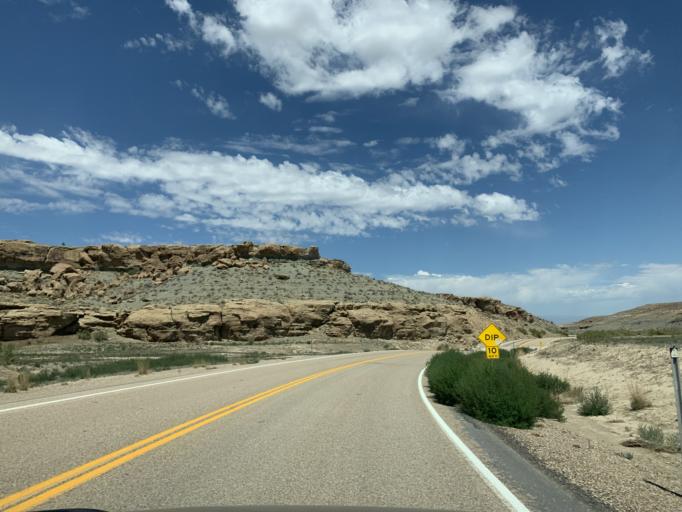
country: US
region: Utah
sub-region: Duchesne County
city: Duchesne
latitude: 40.0222
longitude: -110.1588
